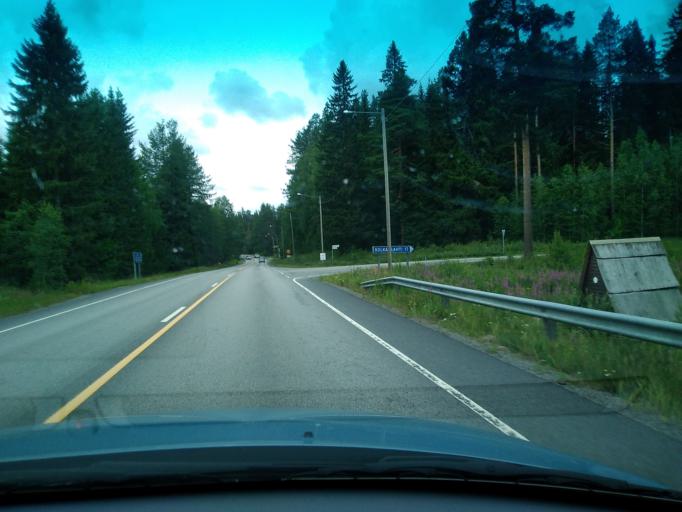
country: FI
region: Central Finland
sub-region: Saarijaervi-Viitasaari
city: Pylkoenmaeki
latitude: 62.6476
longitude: 25.0266
